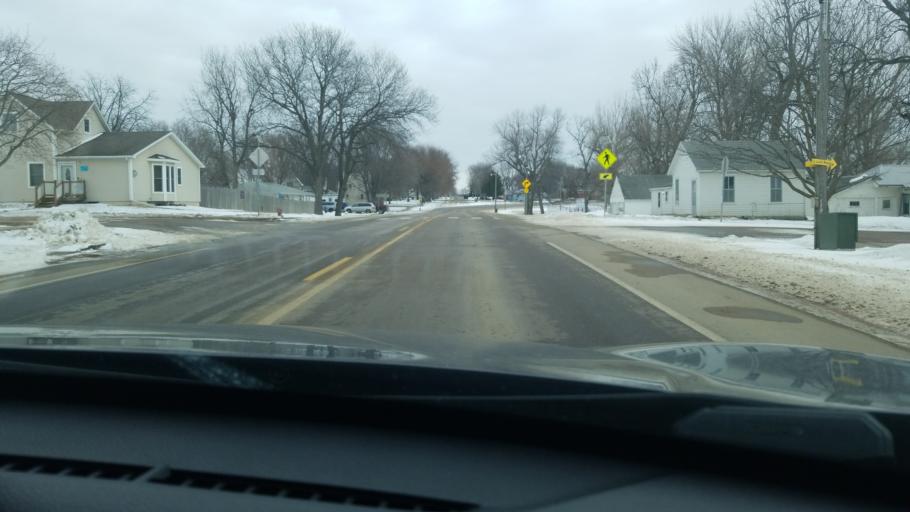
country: US
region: South Dakota
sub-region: Minnehaha County
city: Brandon
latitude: 43.4530
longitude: -96.4331
